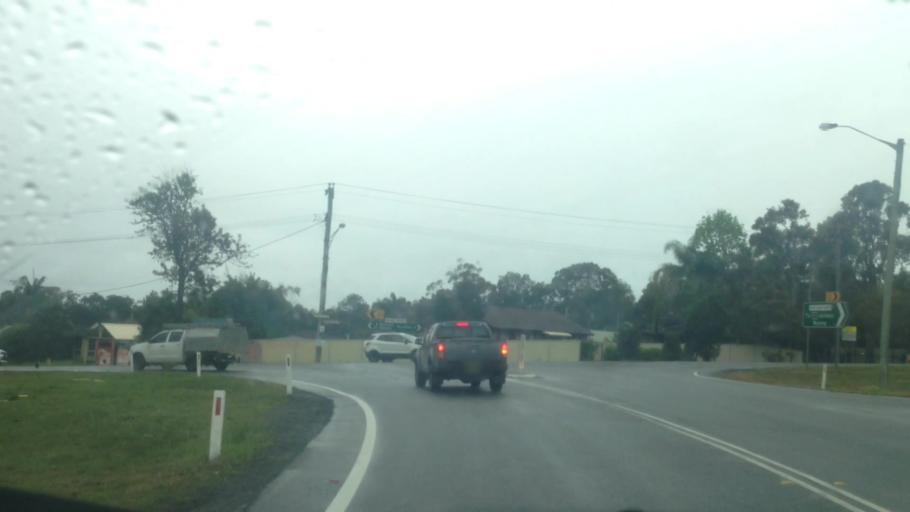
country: AU
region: New South Wales
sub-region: Wyong Shire
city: Charmhaven
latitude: -33.1762
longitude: 151.4808
